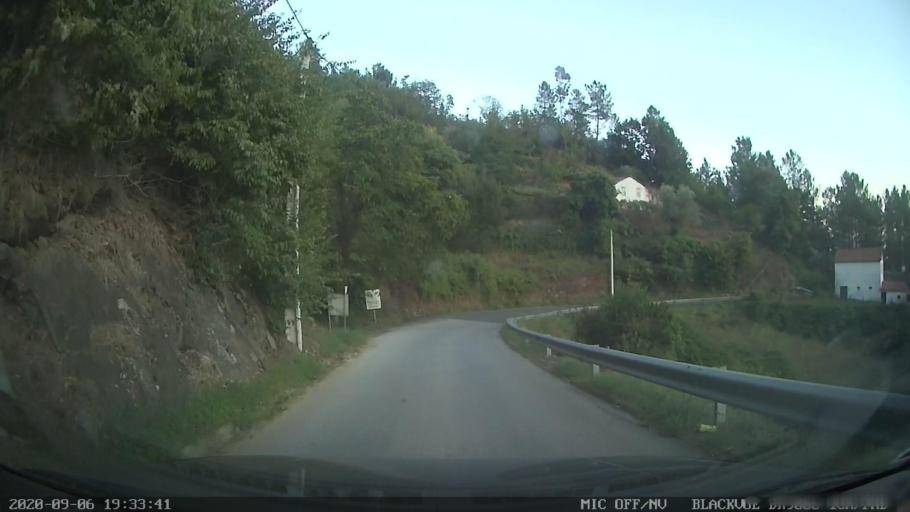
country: PT
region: Vila Real
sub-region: Mesao Frio
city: Mesao Frio
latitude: 41.1749
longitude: -7.8974
